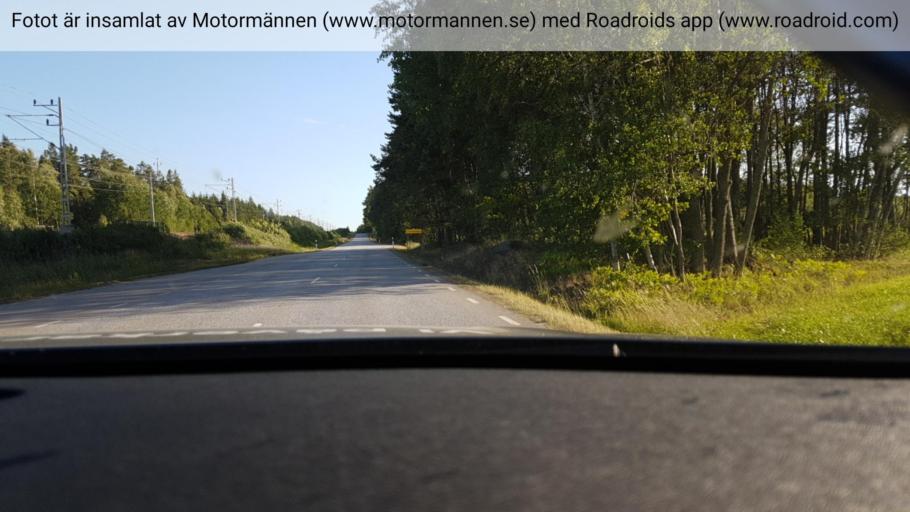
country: SE
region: Vaestra Goetaland
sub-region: Toreboda Kommun
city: Toereboda
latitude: 58.6730
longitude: 14.0982
